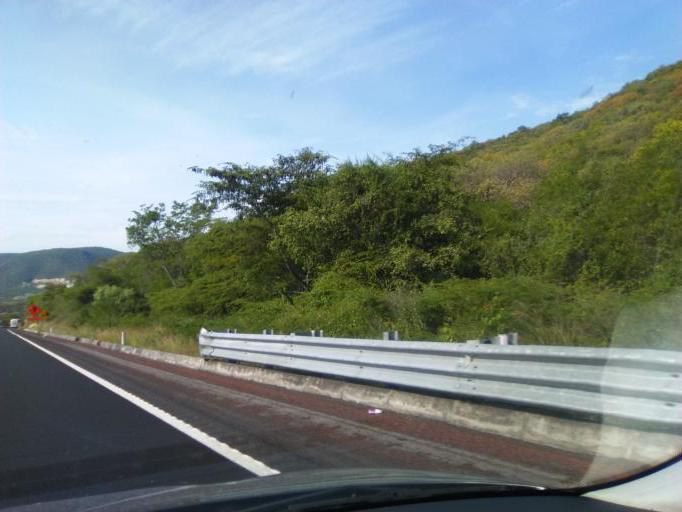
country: MX
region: Morelos
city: Tilzapotla
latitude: 18.4270
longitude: -99.1770
